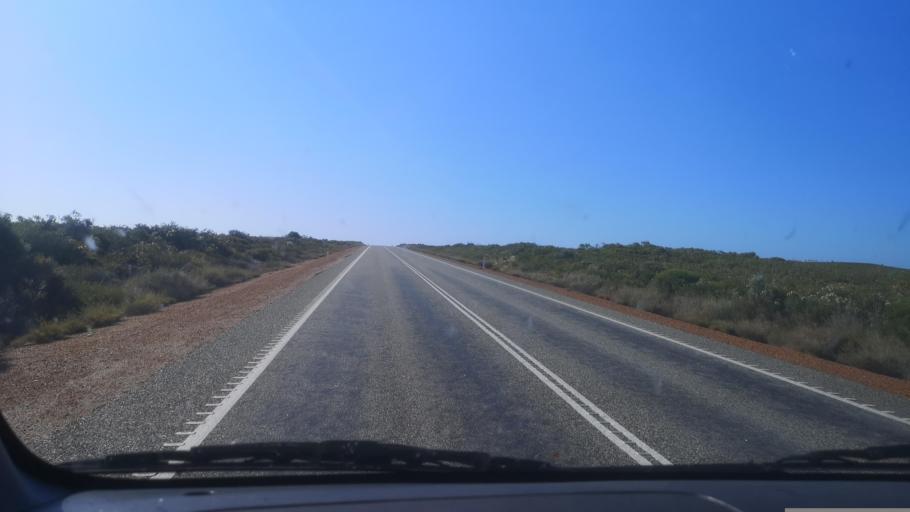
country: AU
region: Western Australia
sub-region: Dandaragan
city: Jurien Bay
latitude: -30.7650
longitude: 115.2022
